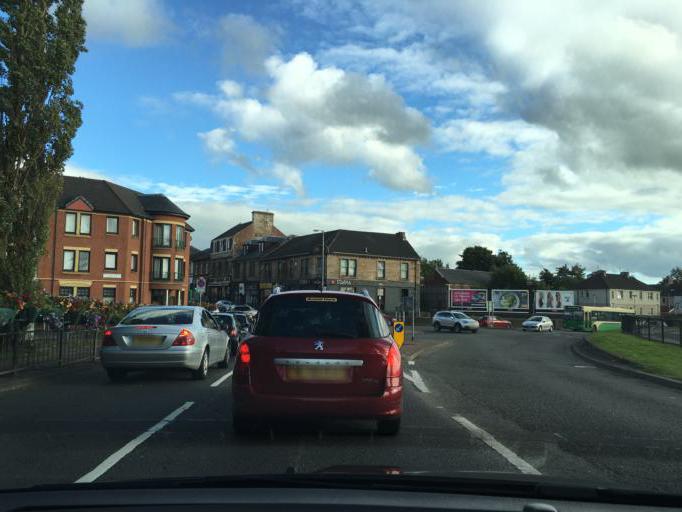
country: GB
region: Scotland
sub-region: North Lanarkshire
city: Motherwell
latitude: 55.7886
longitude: -3.9880
